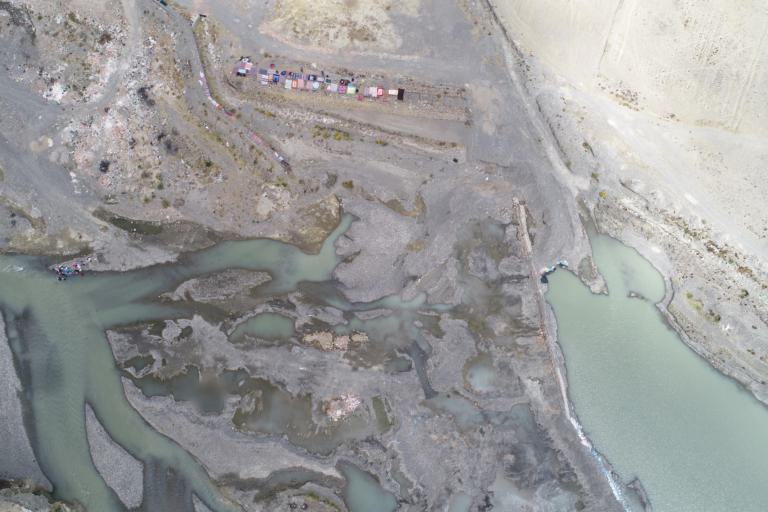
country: BO
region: La Paz
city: Achacachi
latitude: -16.0388
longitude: -68.6822
